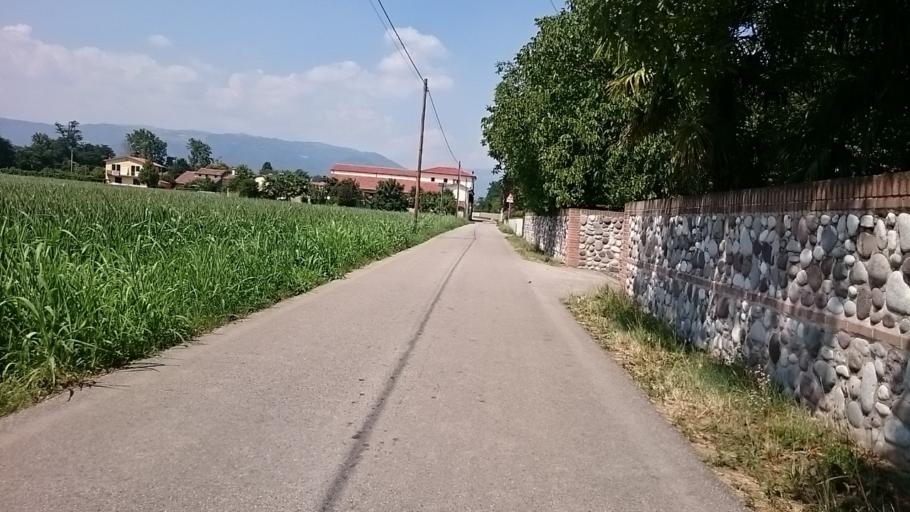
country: IT
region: Veneto
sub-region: Provincia di Vicenza
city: Rosa
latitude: 45.7223
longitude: 11.7366
